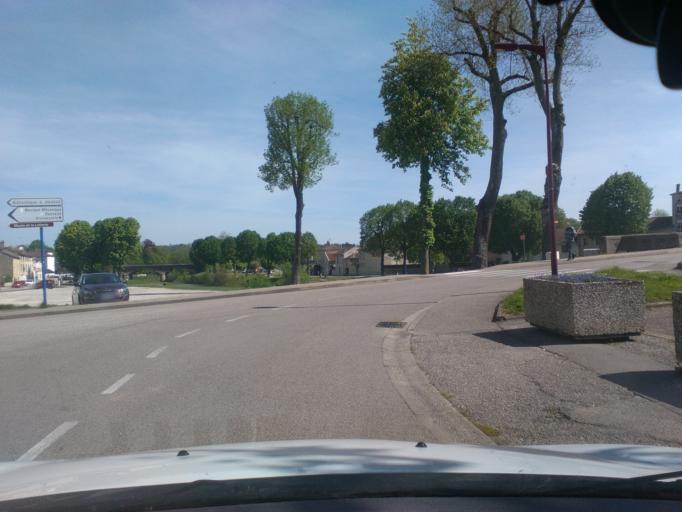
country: FR
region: Lorraine
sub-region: Departement des Vosges
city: Mirecourt
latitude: 48.3004
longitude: 6.1362
